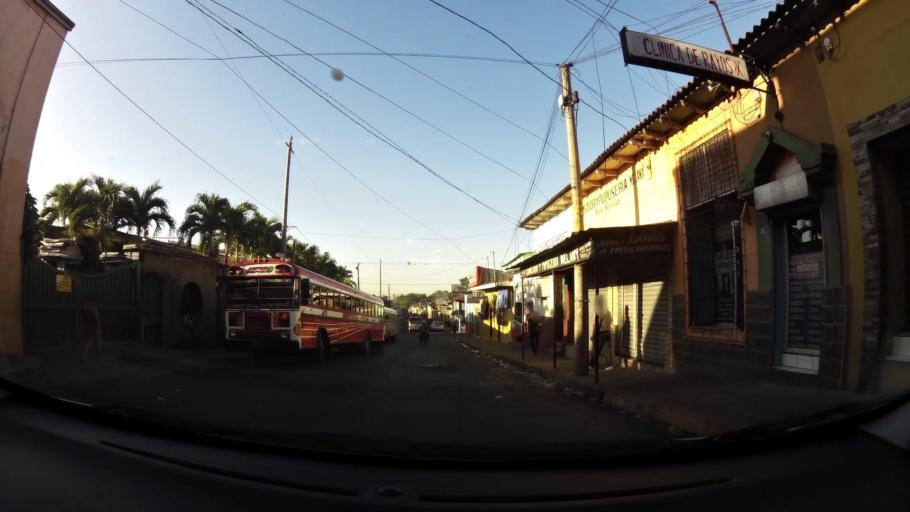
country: SV
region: Sonsonate
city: Sonsonate
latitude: 13.7231
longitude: -89.7299
